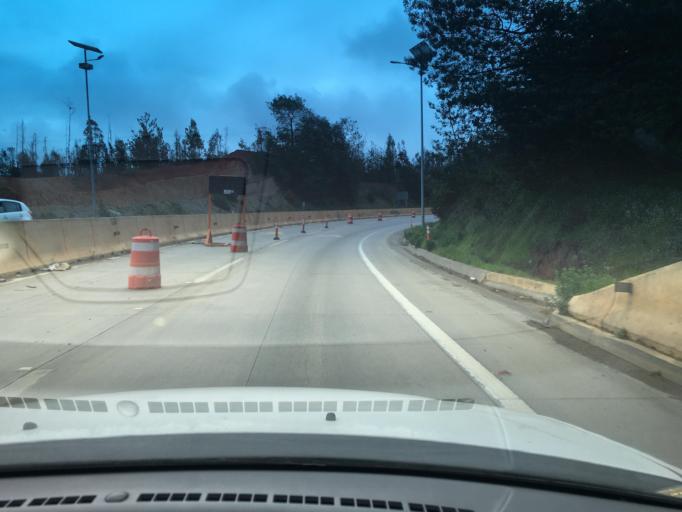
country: CL
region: Valparaiso
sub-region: Provincia de Valparaiso
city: Valparaiso
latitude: -33.0894
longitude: -71.6145
